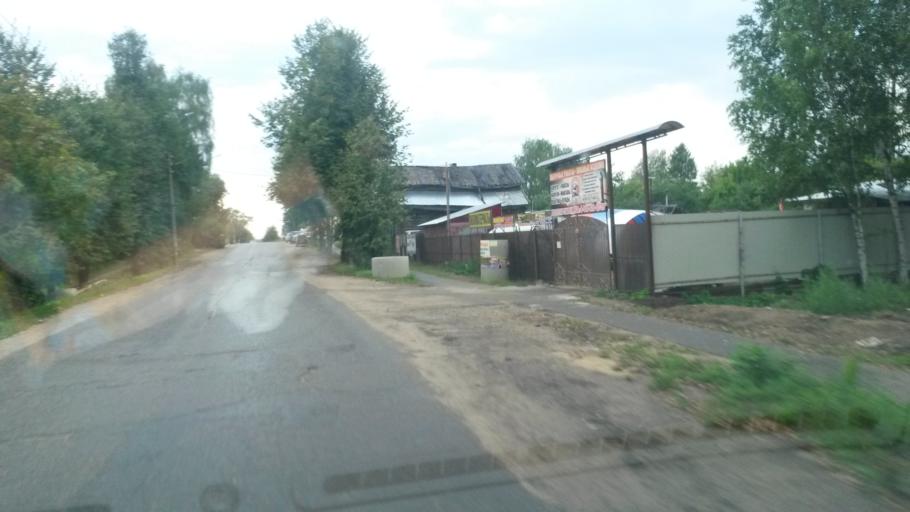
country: RU
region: Jaroslavl
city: Petrovsk
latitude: 57.0108
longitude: 39.2655
